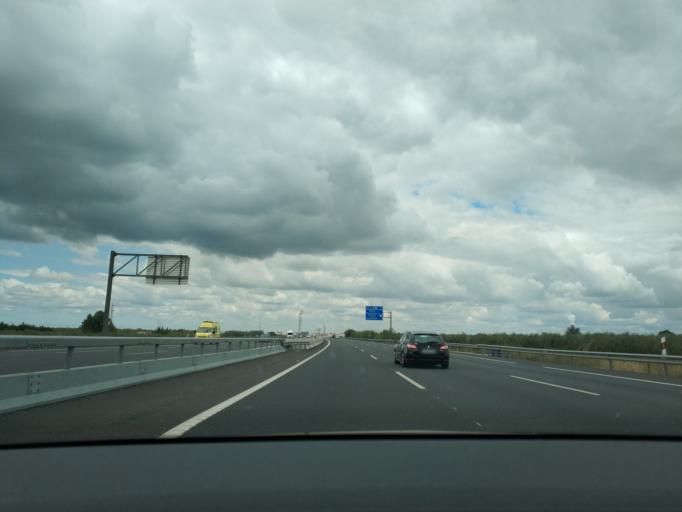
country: ES
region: Andalusia
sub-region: Provincia de Sevilla
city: Benacazon
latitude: 37.3579
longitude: -6.1826
